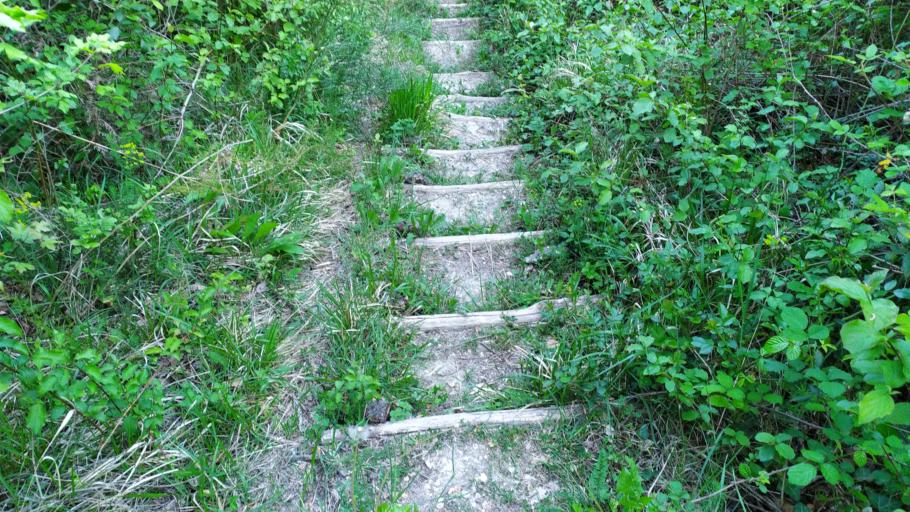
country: IT
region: Emilia-Romagna
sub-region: Provincia di Bologna
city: Borgo Tossignano
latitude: 44.2706
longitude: 11.6080
